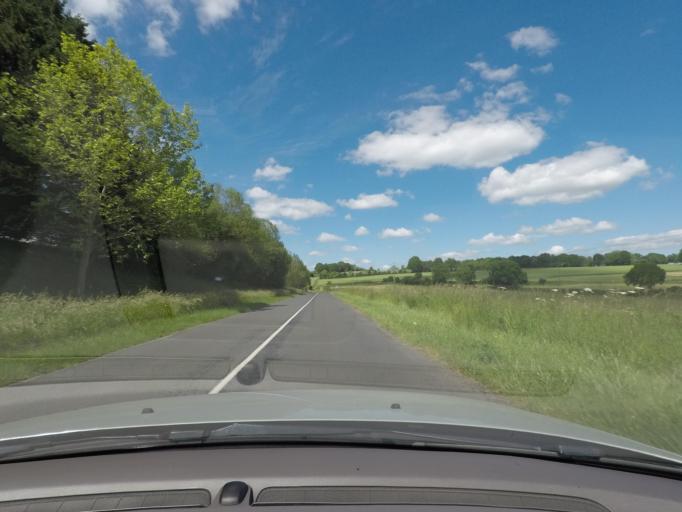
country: FR
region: Lower Normandy
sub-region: Departement de l'Orne
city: Mortagne-au-Perche
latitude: 48.5357
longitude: 0.5582
